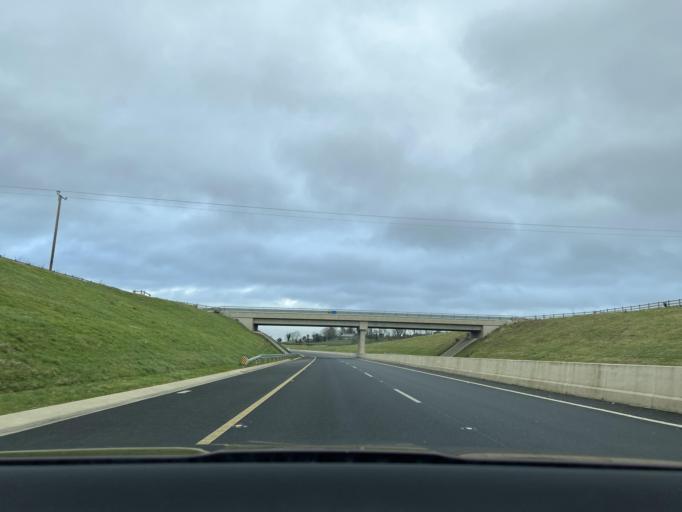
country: IE
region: Leinster
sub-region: Loch Garman
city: Ferns
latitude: 52.5661
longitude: -6.4511
